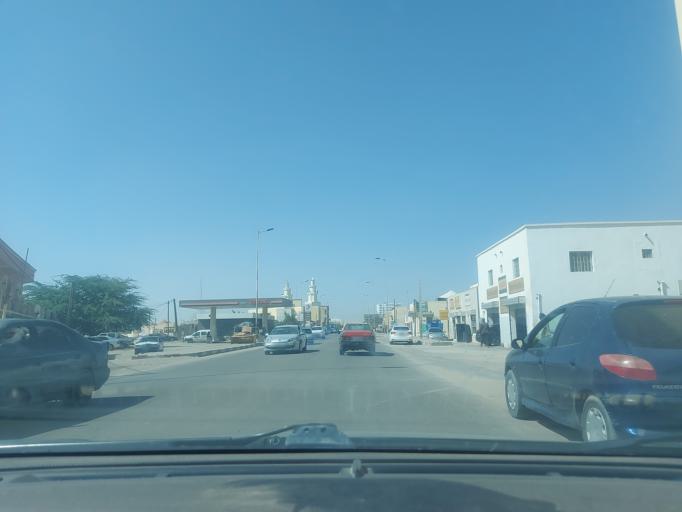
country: MR
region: Nouakchott
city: Nouakchott
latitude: 18.1012
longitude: -15.9571
